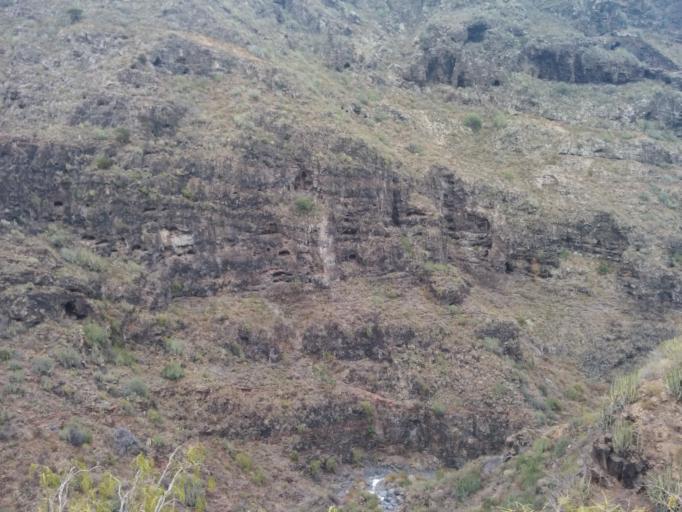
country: ES
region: Canary Islands
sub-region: Provincia de Santa Cruz de Tenerife
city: Adeje
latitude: 28.1303
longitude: -16.7165
